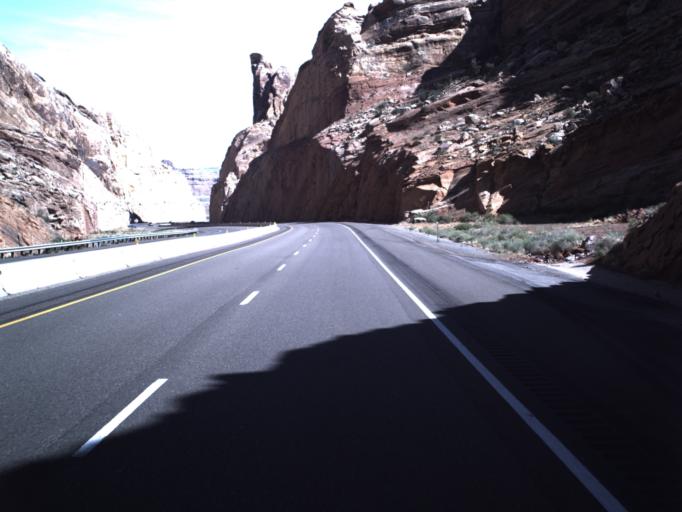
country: US
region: Utah
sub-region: Carbon County
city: East Carbon City
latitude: 38.9234
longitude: -110.4461
